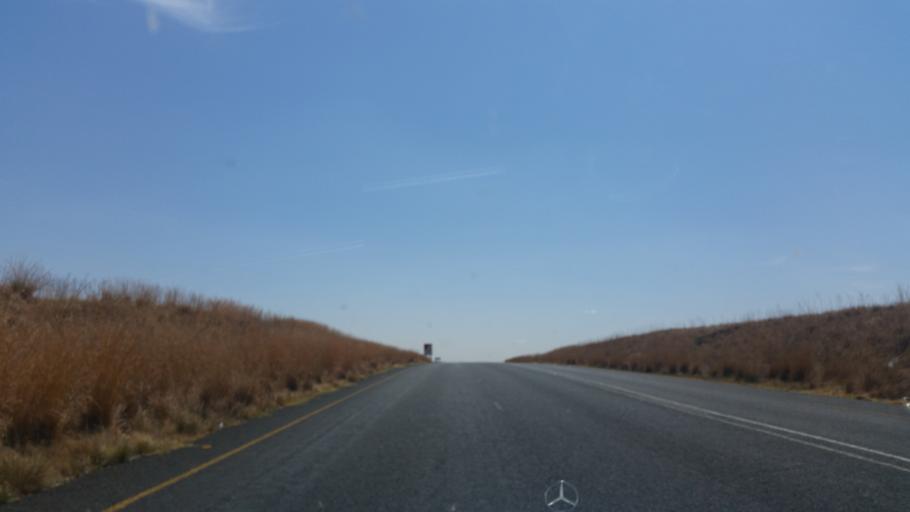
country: ZA
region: Orange Free State
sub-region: Thabo Mofutsanyana District Municipality
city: Phuthaditjhaba
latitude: -28.1696
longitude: 28.6838
